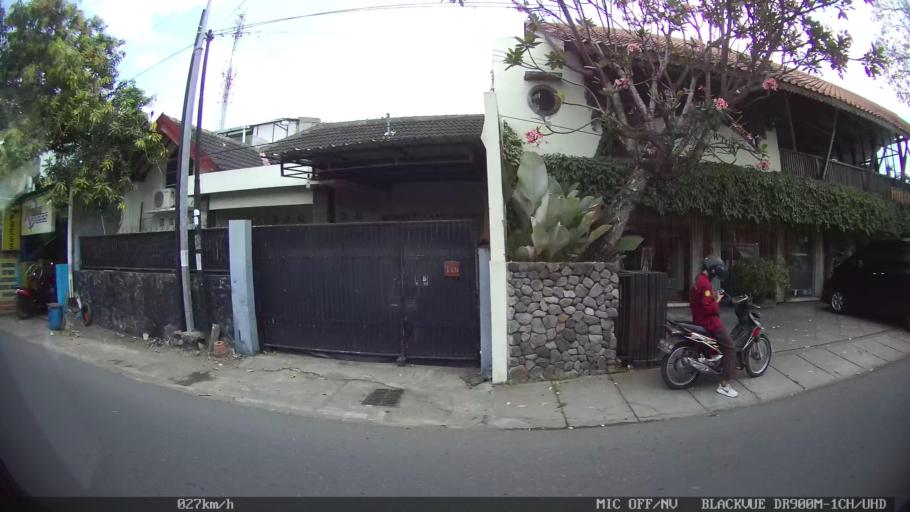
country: ID
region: Daerah Istimewa Yogyakarta
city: Kasihan
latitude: -7.8174
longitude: 110.3484
